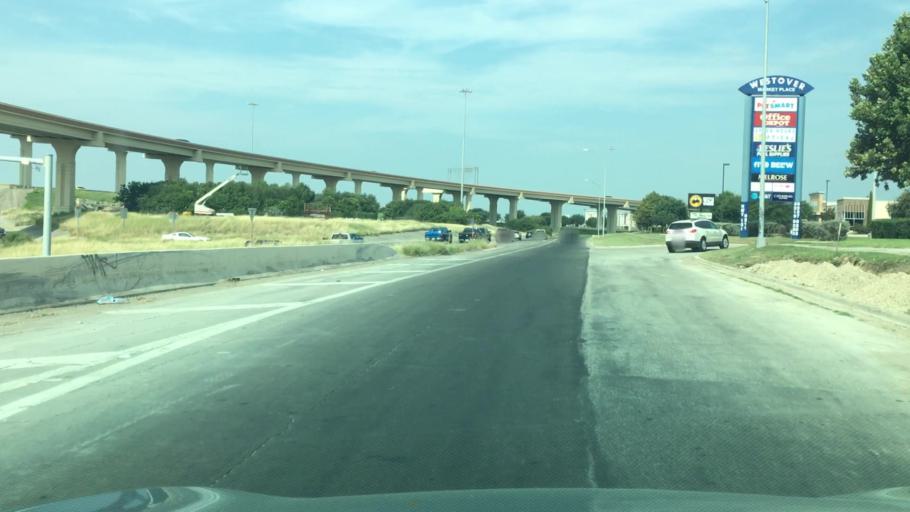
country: US
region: Texas
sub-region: Bexar County
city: Lackland Air Force Base
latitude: 29.4363
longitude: -98.6450
